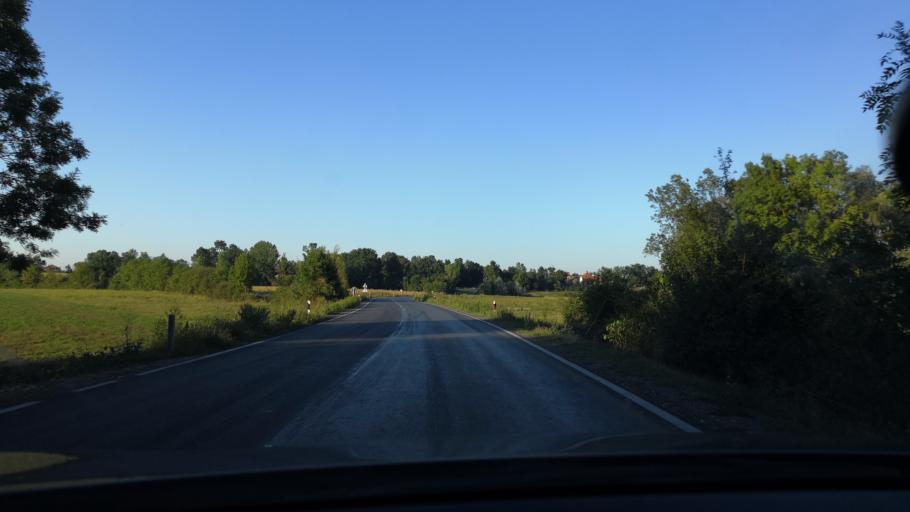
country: RS
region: Central Serbia
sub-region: Belgrade
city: Mladenovac
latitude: 44.3658
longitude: 20.6427
